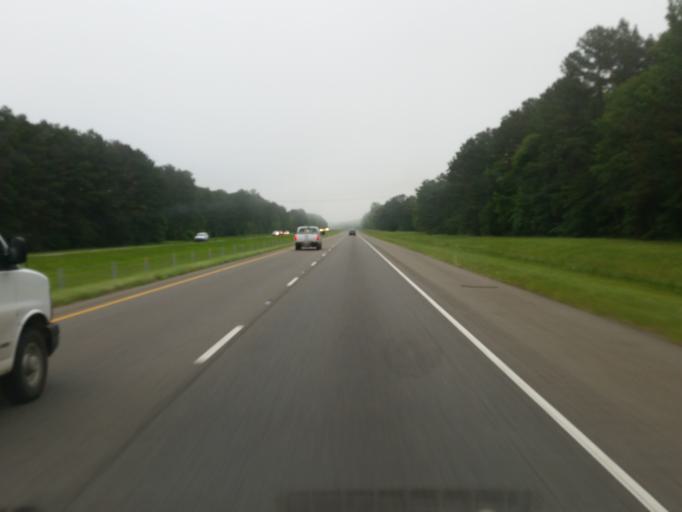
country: US
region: Louisiana
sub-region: Bossier Parish
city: Haughton
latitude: 32.5768
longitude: -93.4654
